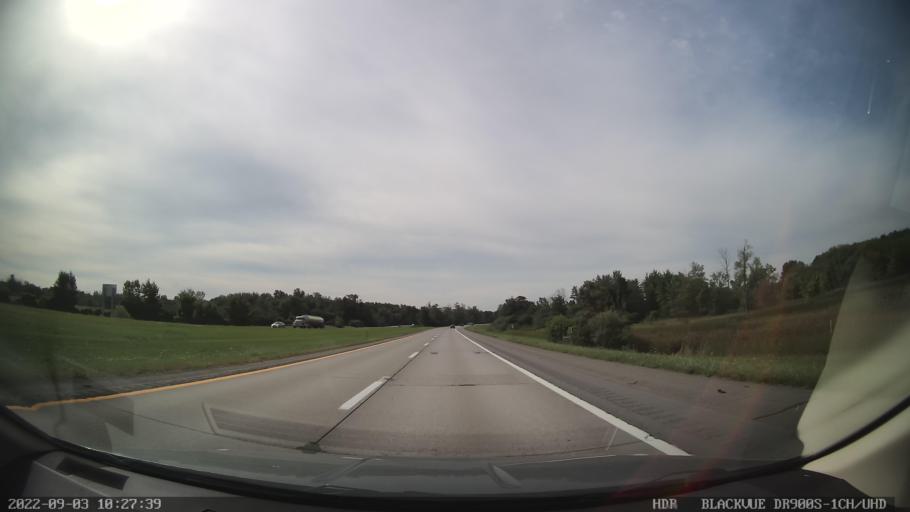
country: US
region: New York
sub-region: Livingston County
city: Livonia
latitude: 42.8131
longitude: -77.7380
